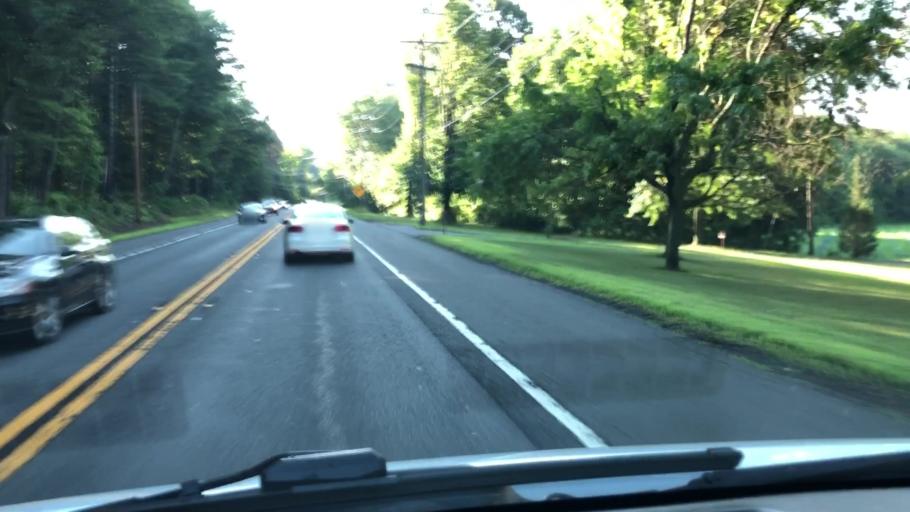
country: US
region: Massachusetts
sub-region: Hampshire County
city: North Amherst
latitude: 42.4490
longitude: -72.5587
